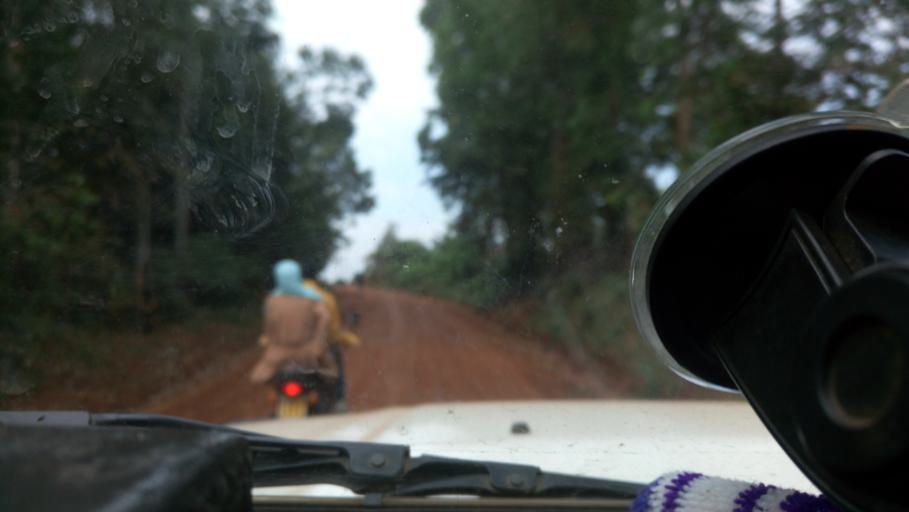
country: KE
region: Kericho
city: Litein
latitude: -0.6200
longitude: 35.2017
